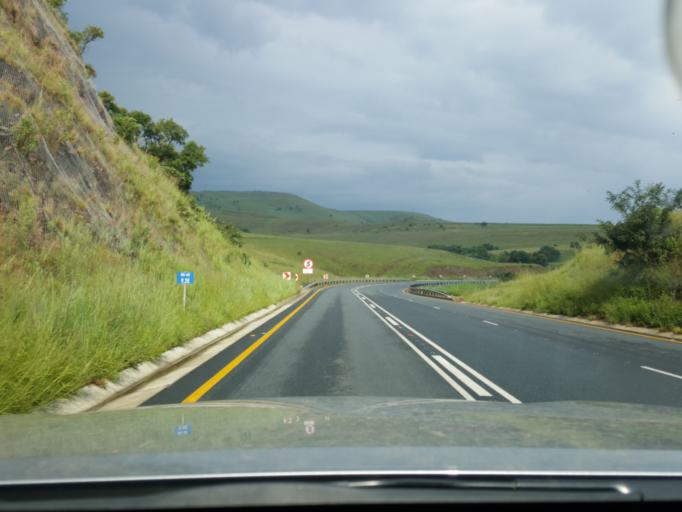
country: ZA
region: Mpumalanga
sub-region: Nkangala District Municipality
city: Belfast
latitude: -25.6261
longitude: 30.3365
